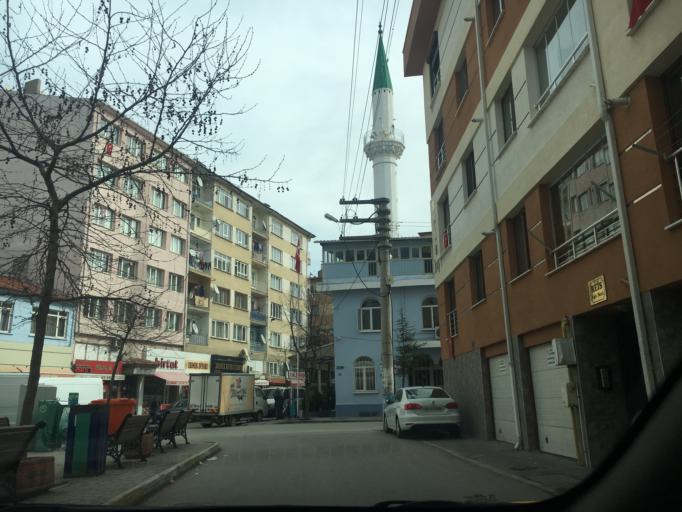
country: TR
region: Eskisehir
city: Eskisehir
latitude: 39.7733
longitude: 30.5082
